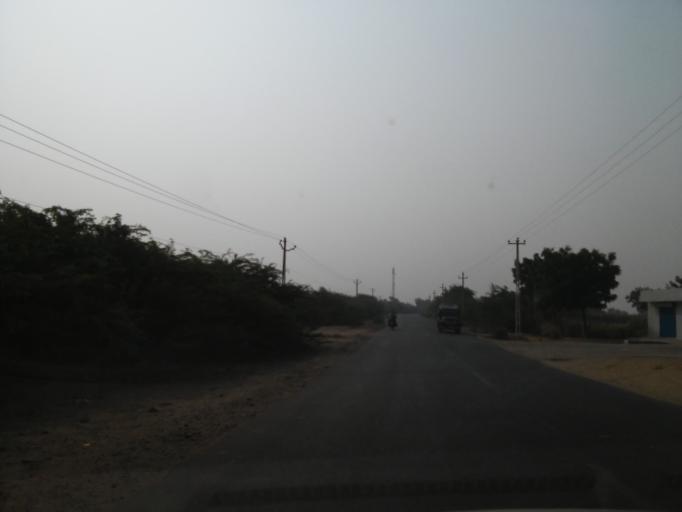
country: IN
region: Gujarat
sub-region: Kachchh
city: Bhuj
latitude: 23.8374
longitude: 69.7299
